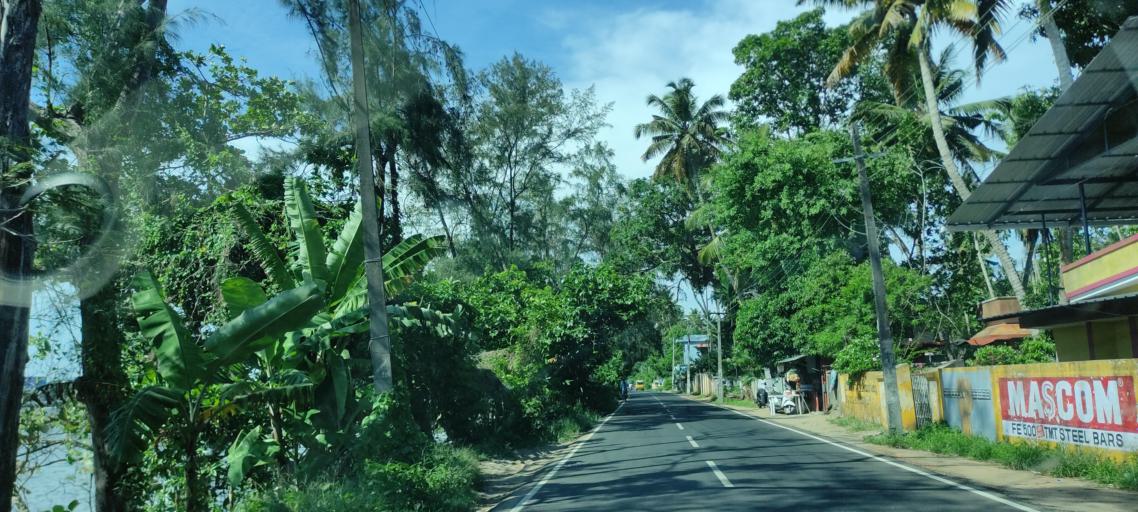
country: IN
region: Kerala
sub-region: Alappuzha
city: Mavelikara
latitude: 9.3124
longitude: 76.3849
